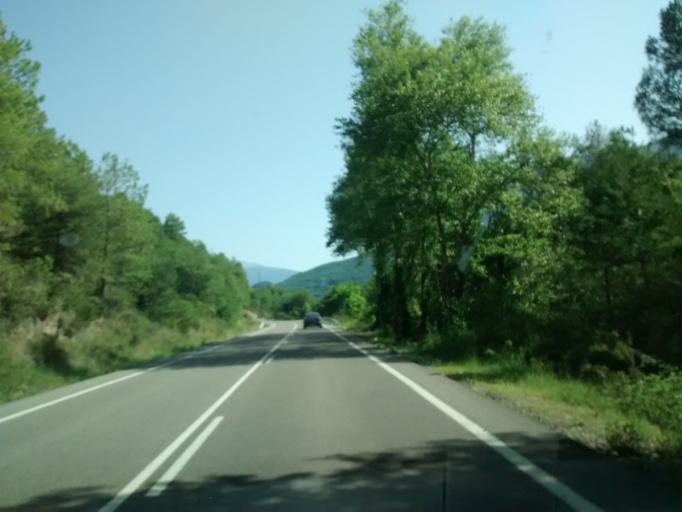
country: ES
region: Aragon
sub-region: Provincia de Huesca
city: Labuerda
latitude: 42.4737
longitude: 0.1473
